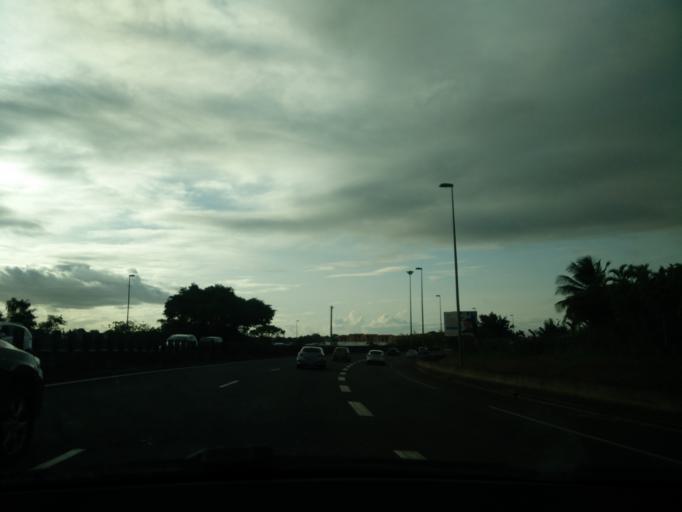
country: GP
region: Guadeloupe
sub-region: Guadeloupe
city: Baie-Mahault
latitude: 16.2481
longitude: -61.5890
